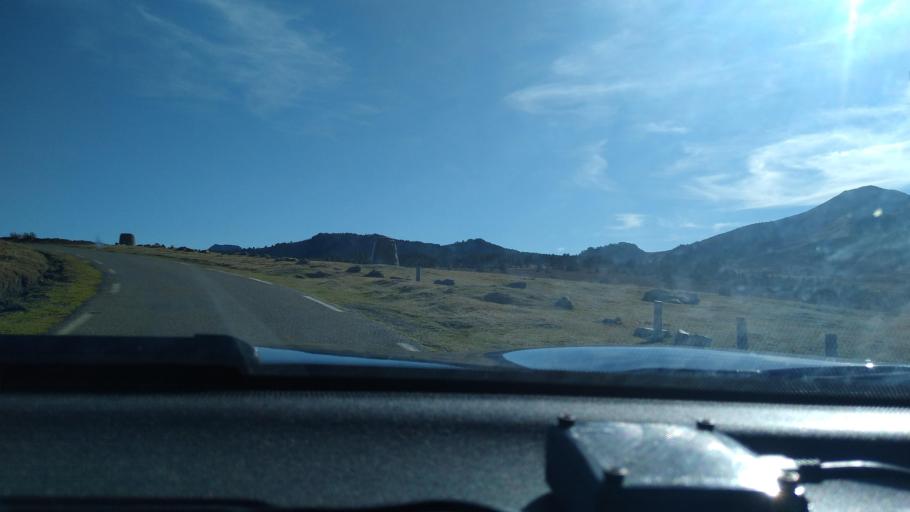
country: FR
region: Midi-Pyrenees
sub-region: Departement de l'Ariege
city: Ax-les-Thermes
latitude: 42.7322
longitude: 1.9881
